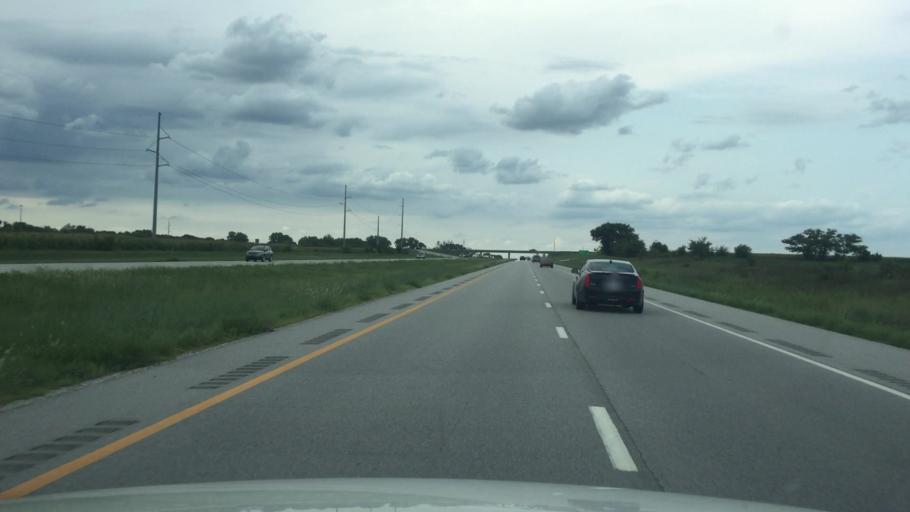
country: US
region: Kansas
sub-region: Miami County
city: Louisburg
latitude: 38.7175
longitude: -94.6763
